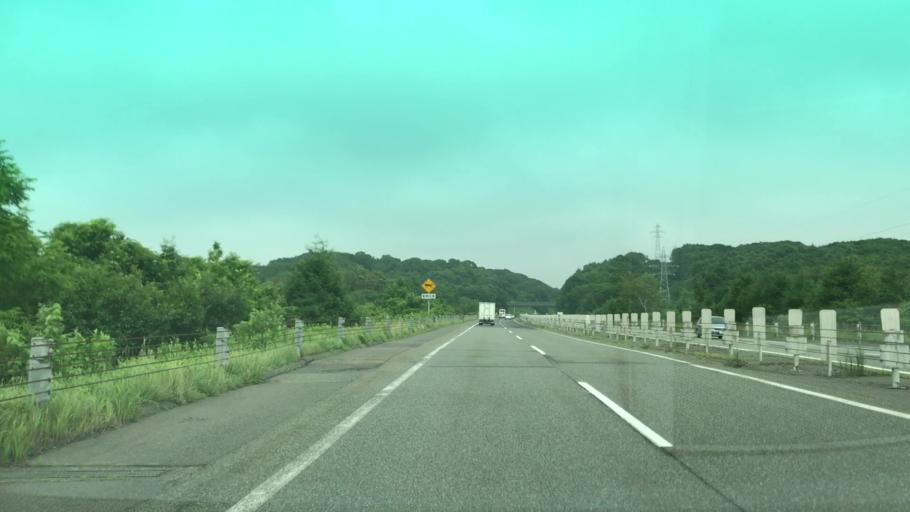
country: JP
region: Hokkaido
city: Tomakomai
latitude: 42.6589
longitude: 141.5767
